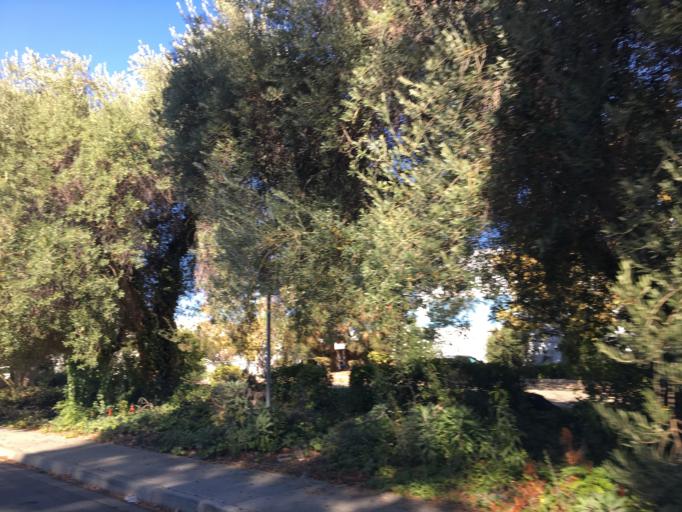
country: US
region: California
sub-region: Santa Clara County
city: Milpitas
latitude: 37.4951
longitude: -121.9263
